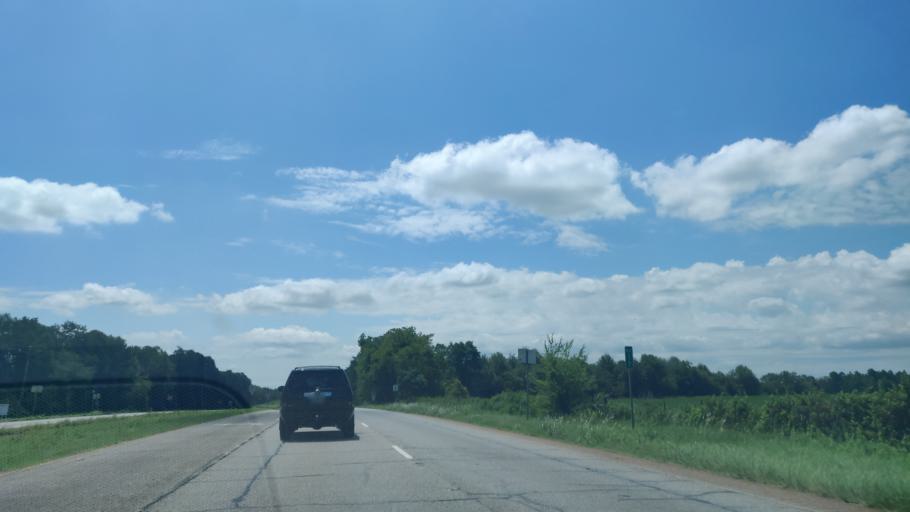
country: US
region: Georgia
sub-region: Stewart County
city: Richland
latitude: 32.0109
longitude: -84.6558
